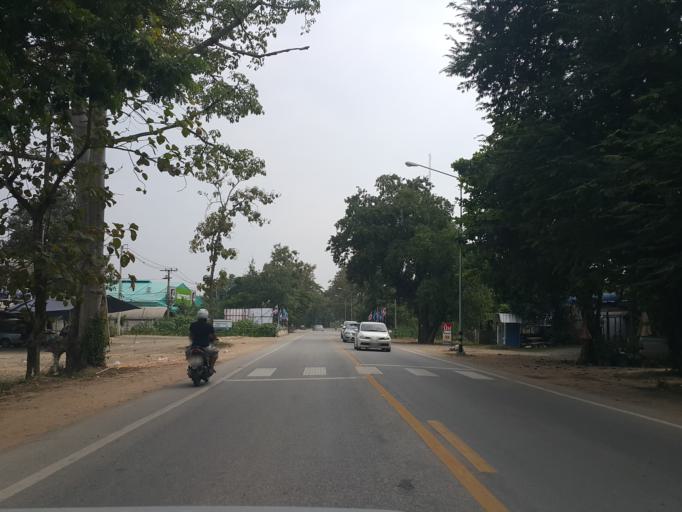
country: TH
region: Chiang Mai
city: Mae Taeng
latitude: 18.9955
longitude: 98.9774
